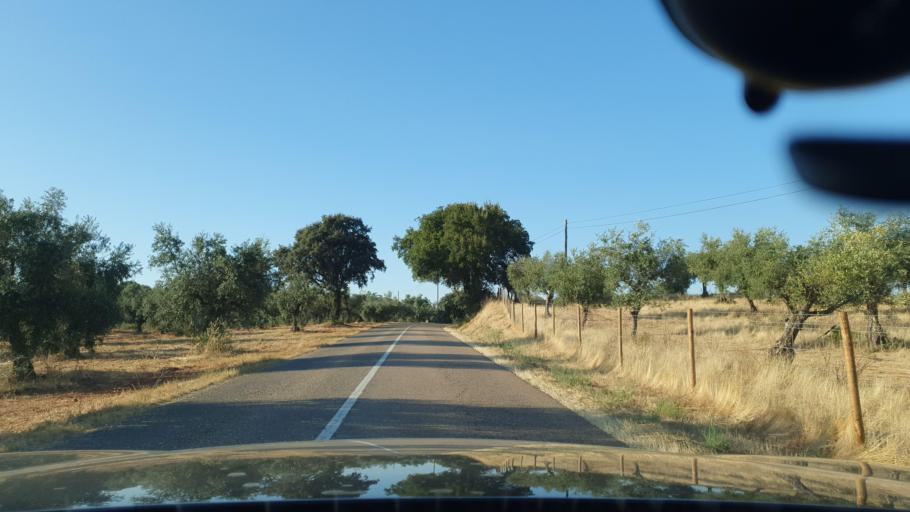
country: PT
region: Evora
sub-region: Estremoz
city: Estremoz
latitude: 38.9319
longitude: -7.6672
